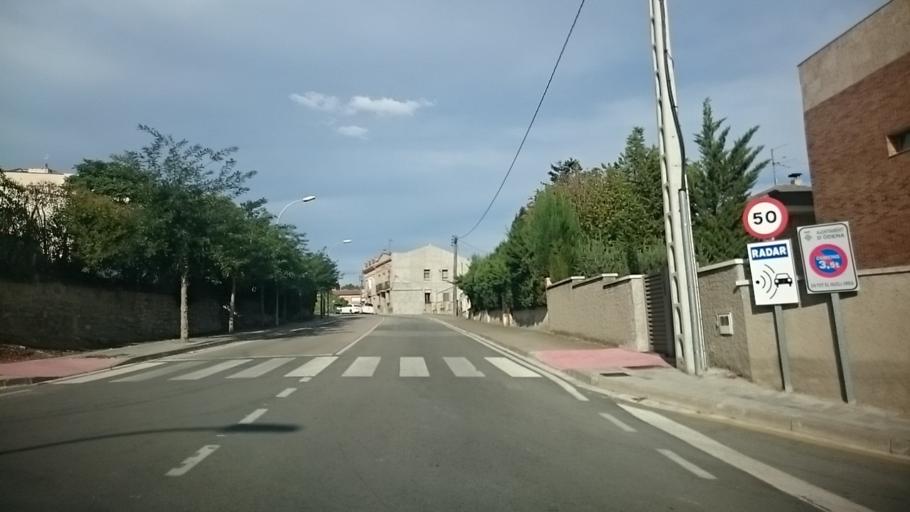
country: ES
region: Catalonia
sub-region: Provincia de Barcelona
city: Odena
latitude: 41.6031
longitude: 1.6394
